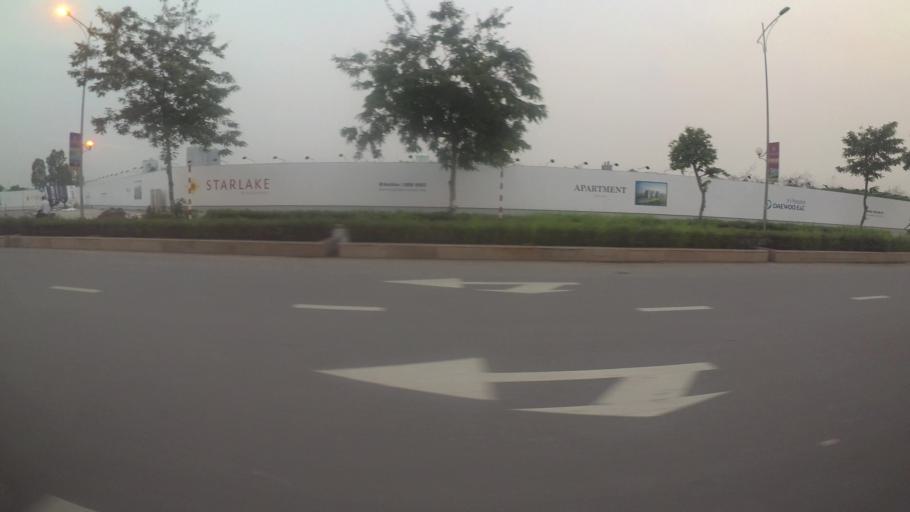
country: VN
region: Ha Noi
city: Tay Ho
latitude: 21.0625
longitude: 105.8003
